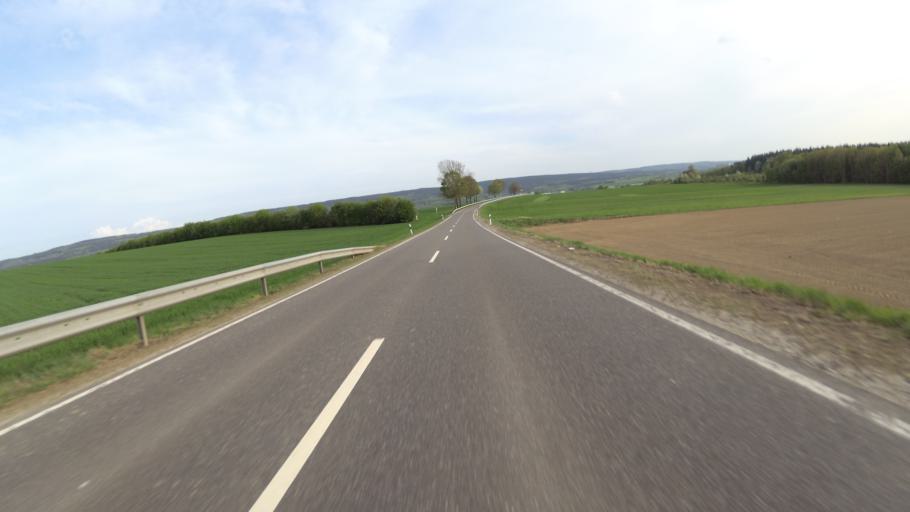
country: DE
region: Rheinland-Pfalz
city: Morbach
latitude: 49.8273
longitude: 7.1248
